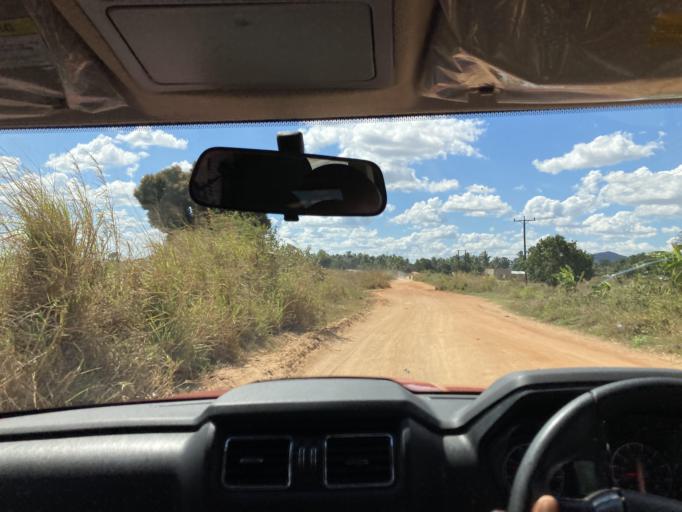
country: MZ
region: Cabo Delgado
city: Montepuez
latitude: -13.1487
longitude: 38.9913
